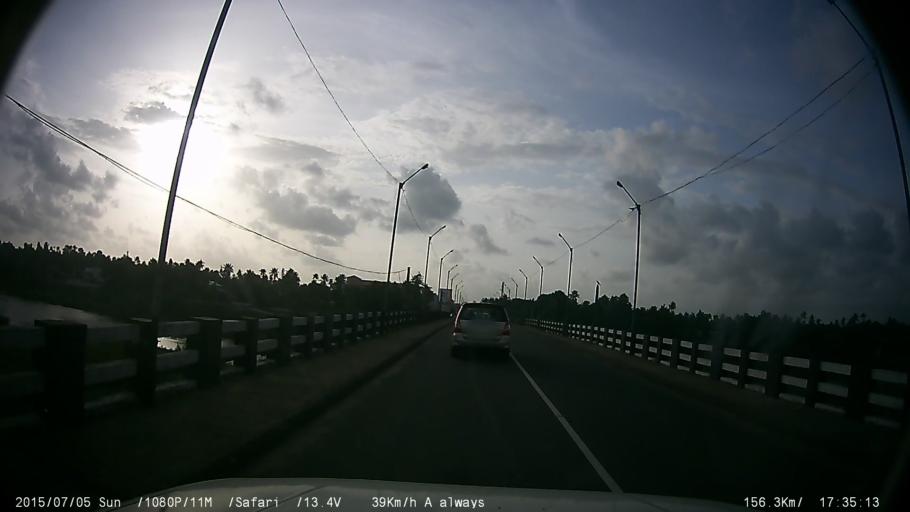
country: IN
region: Kerala
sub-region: Ernakulam
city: Angamali
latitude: 10.1609
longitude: 76.4416
